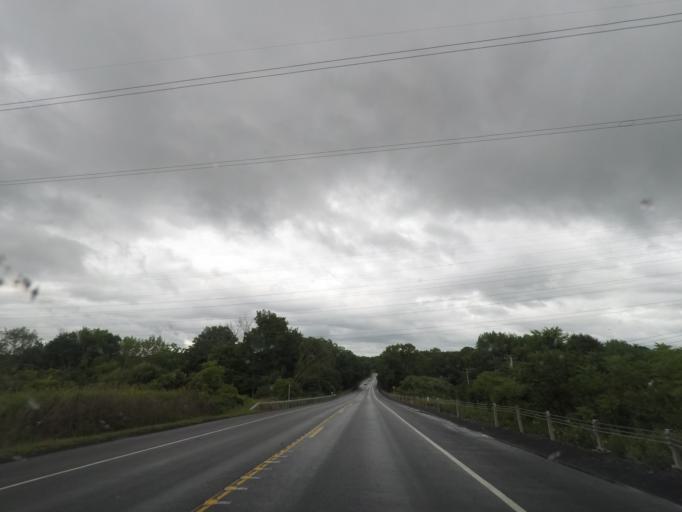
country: US
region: New York
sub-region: Rensselaer County
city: Hampton Manor
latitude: 42.6204
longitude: -73.7125
